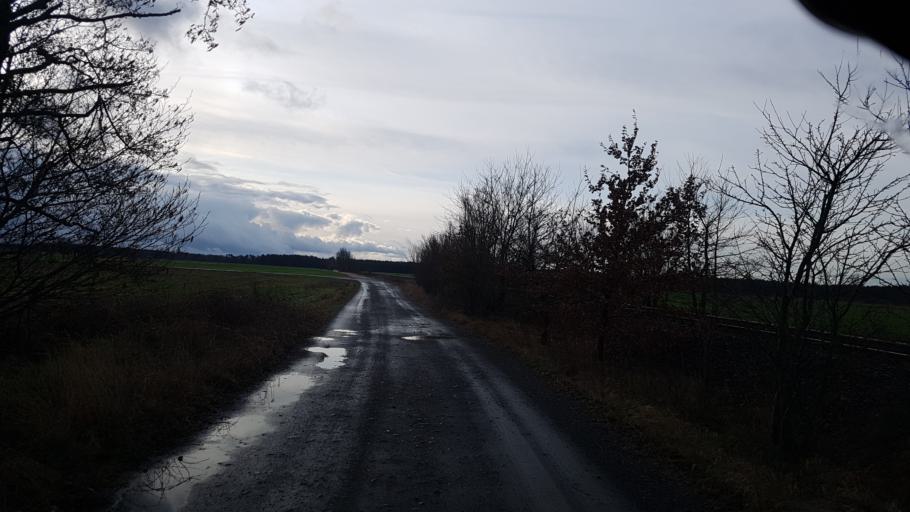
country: DE
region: Brandenburg
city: Herzberg
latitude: 51.6752
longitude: 13.2391
